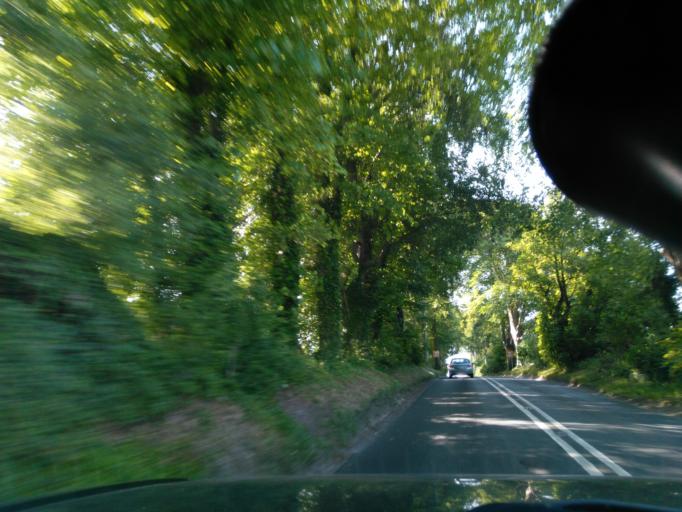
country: GB
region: England
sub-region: Wiltshire
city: Woodford
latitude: 51.1039
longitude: -1.8416
